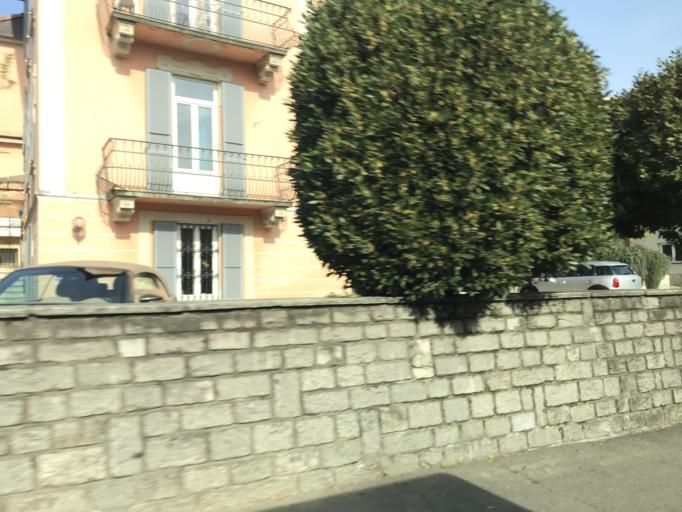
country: CH
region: Ticino
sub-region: Lugano District
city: Sorengo
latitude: 45.9982
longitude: 8.9388
